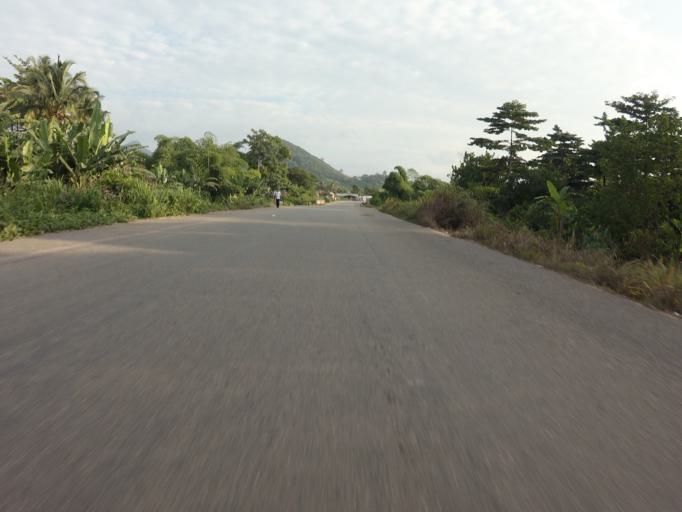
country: GH
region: Volta
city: Kpandu
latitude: 6.8974
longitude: 0.4328
